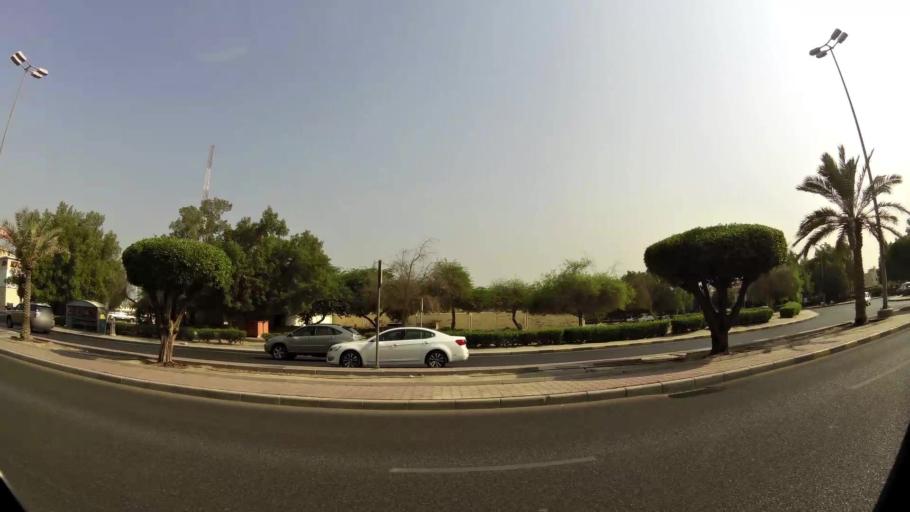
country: KW
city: Bayan
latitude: 29.2984
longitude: 48.0515
